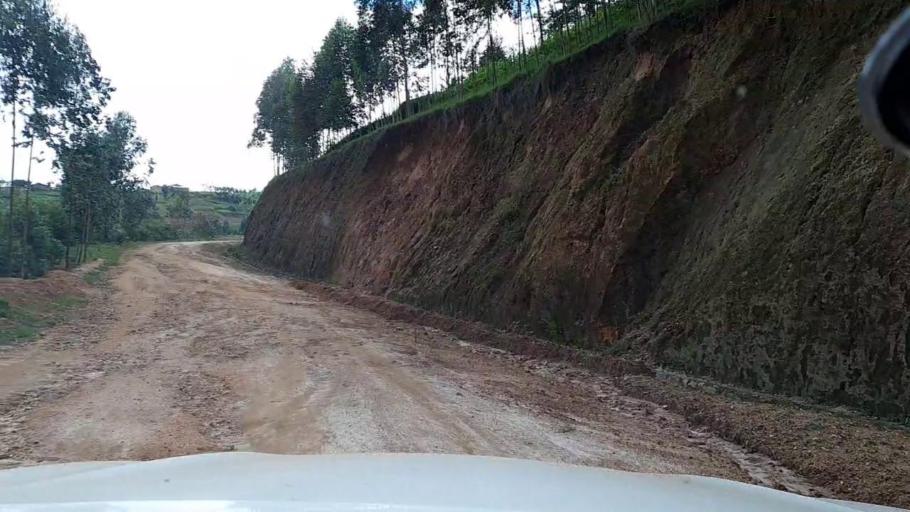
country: RW
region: Southern Province
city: Nzega
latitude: -2.6958
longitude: 29.4408
